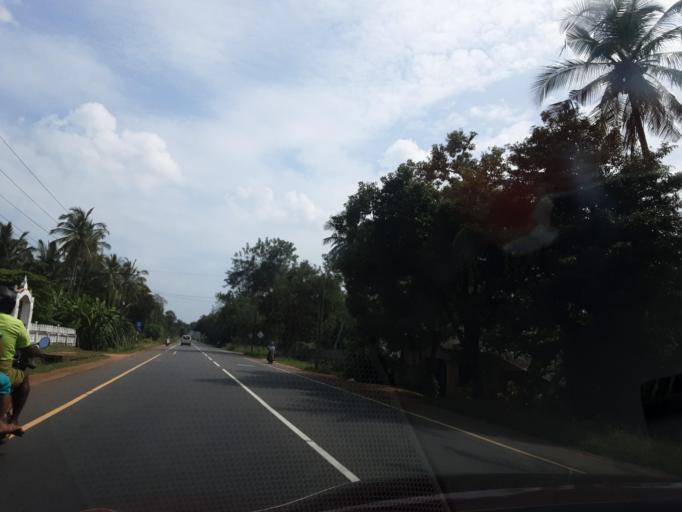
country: LK
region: North Central
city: Anuradhapura
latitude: 8.5044
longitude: 80.5091
